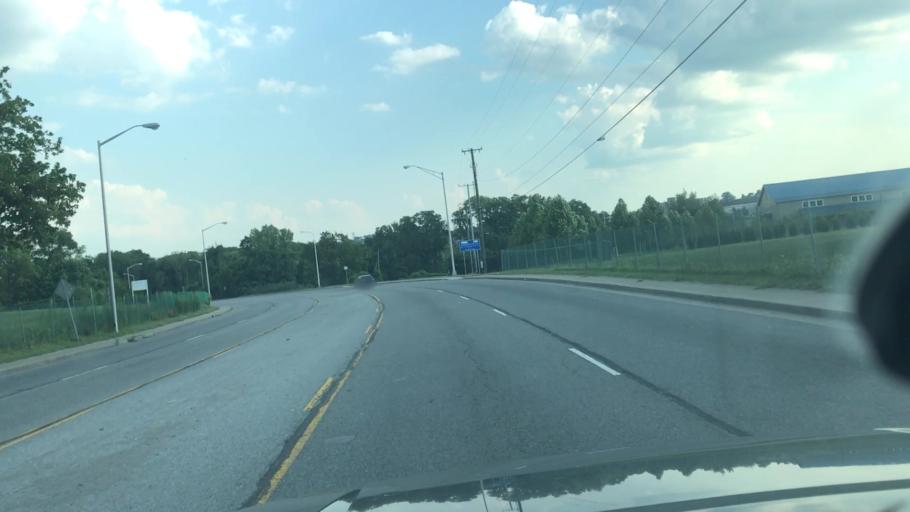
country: US
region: Tennessee
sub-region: Davidson County
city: Nashville
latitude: 36.1773
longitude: -86.8246
